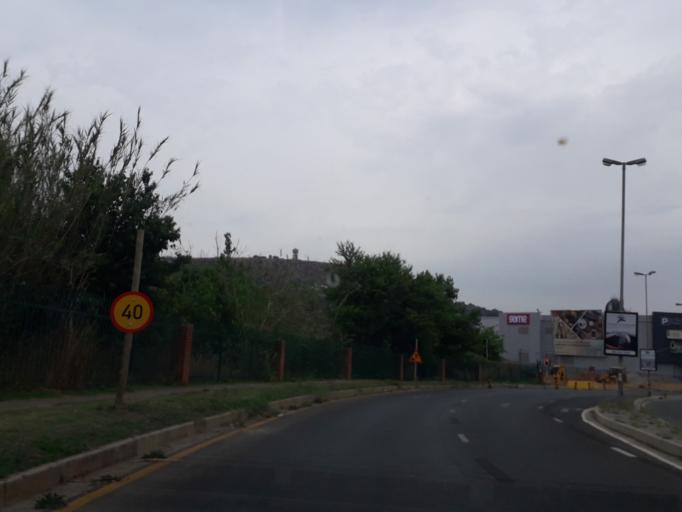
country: ZA
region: Gauteng
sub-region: City of Johannesburg Metropolitan Municipality
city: Johannesburg
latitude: -26.1294
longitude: 27.9789
